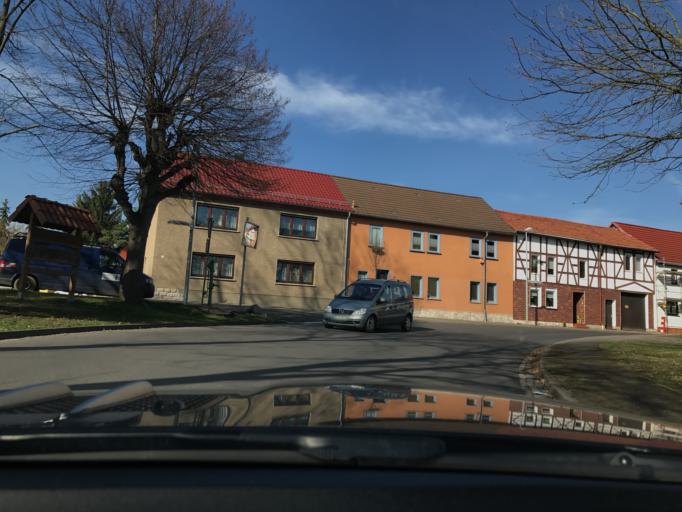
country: DE
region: Thuringia
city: Bad Langensalza
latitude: 51.1389
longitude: 10.6329
